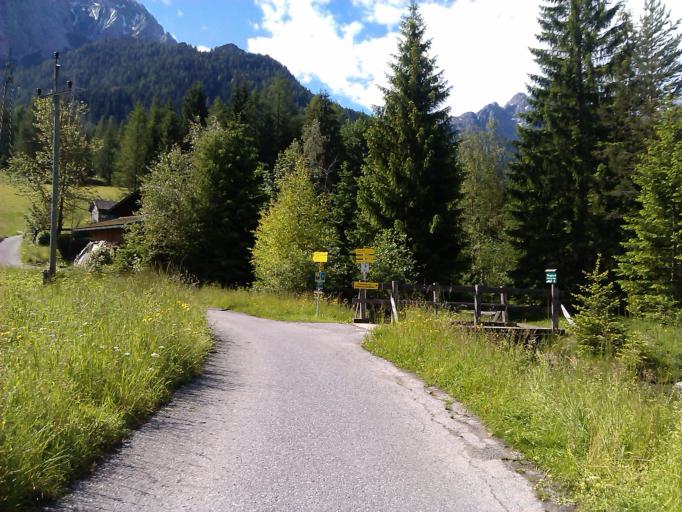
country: AT
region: Tyrol
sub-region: Politischer Bezirk Reutte
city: Biberwier
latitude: 47.3791
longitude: 10.8942
